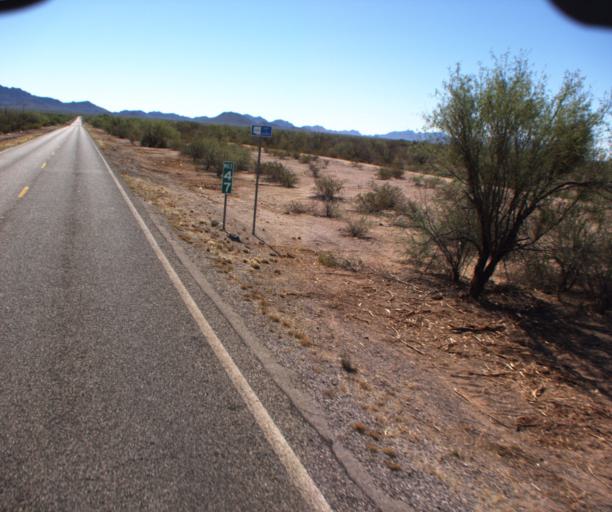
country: US
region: Arizona
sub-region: Pima County
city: Ajo
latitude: 32.3345
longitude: -112.7907
